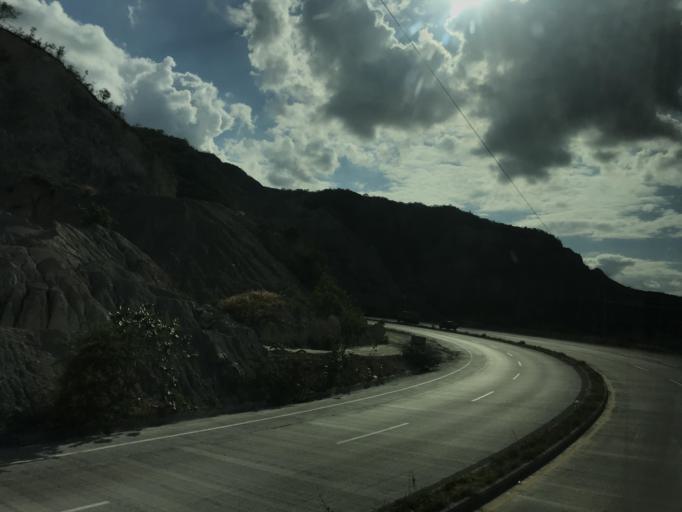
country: GT
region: El Progreso
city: Guastatoya
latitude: 14.8477
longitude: -90.1250
